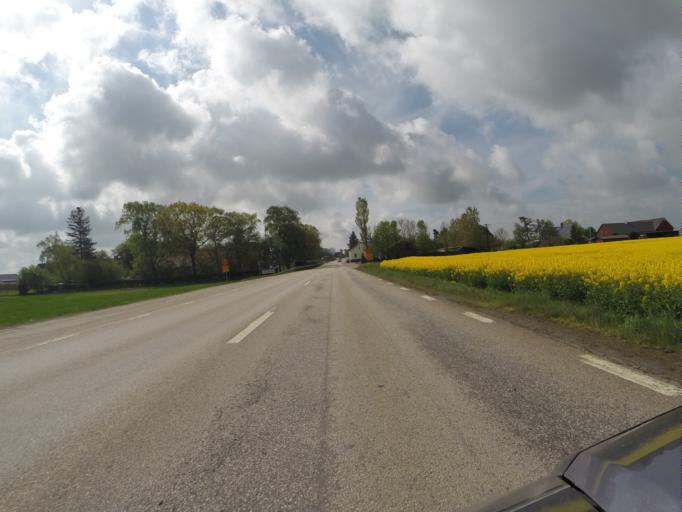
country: SE
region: Skane
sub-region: Landskrona
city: Asmundtorp
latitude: 55.9565
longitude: 12.9459
